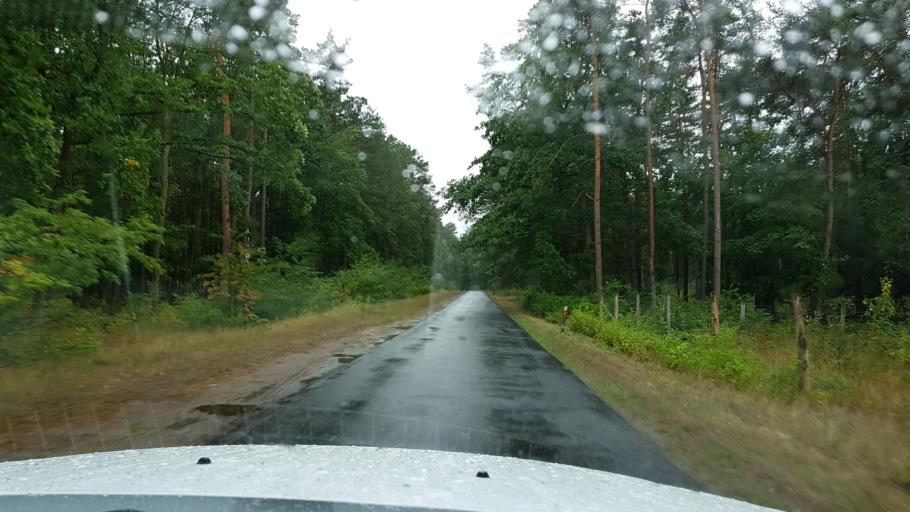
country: DE
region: Brandenburg
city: Schoneberg
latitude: 52.9637
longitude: 14.2025
